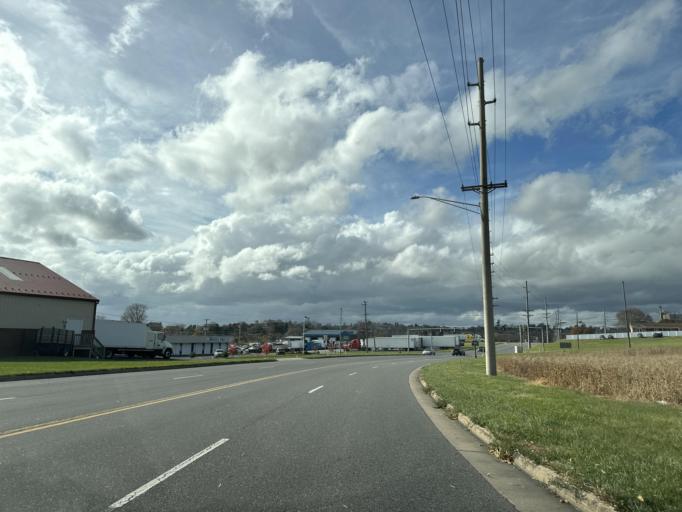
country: US
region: Virginia
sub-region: City of Harrisonburg
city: Harrisonburg
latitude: 38.4667
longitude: -78.8611
